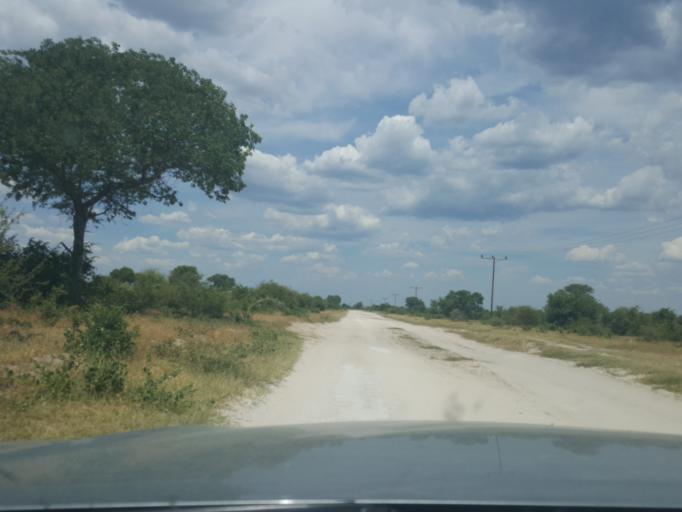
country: BW
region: North West
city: Shakawe
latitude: -18.5064
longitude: 22.1373
